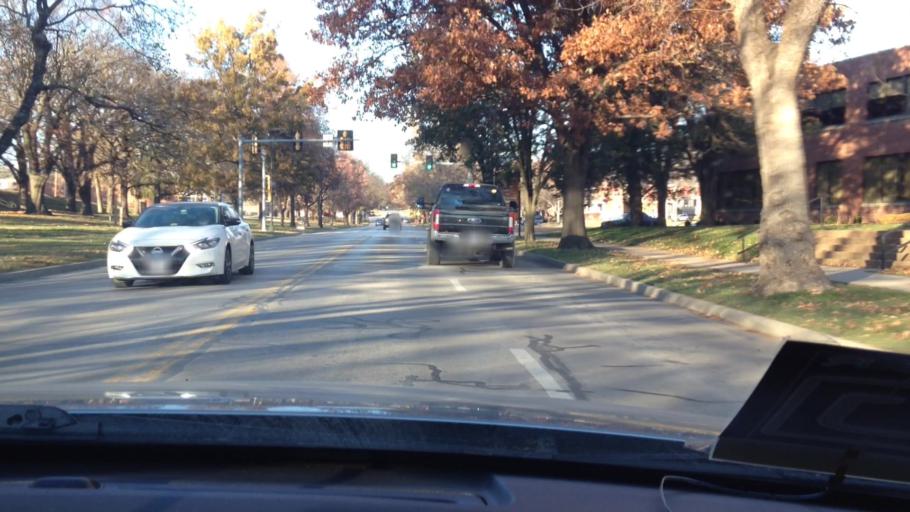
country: US
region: Kansas
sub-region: Leavenworth County
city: Leavenworth
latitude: 39.3481
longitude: -94.9193
